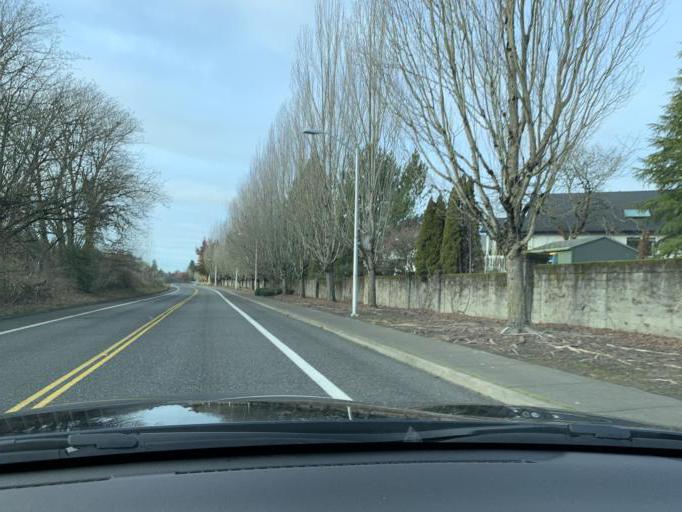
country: US
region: Washington
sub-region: Clark County
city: Mill Plain
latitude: 45.5958
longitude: -122.5173
